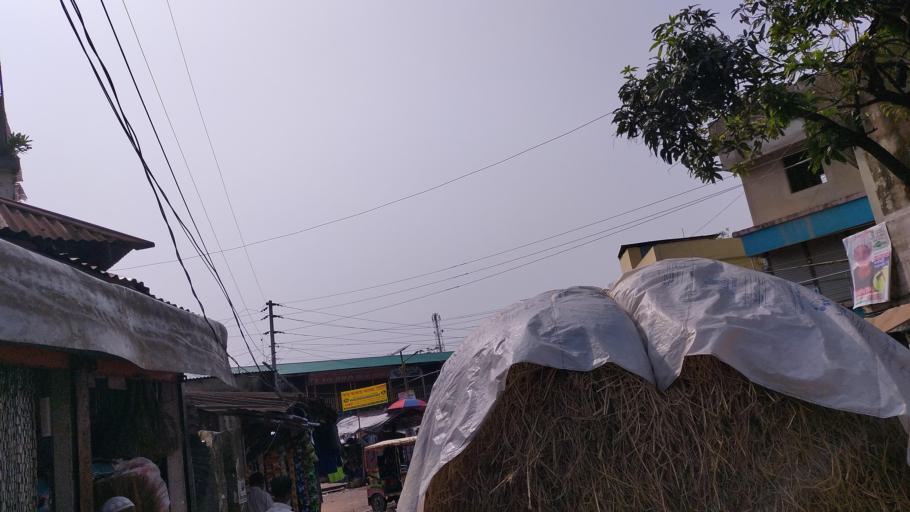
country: BD
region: Dhaka
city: Netrakona
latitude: 25.0774
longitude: 90.8884
